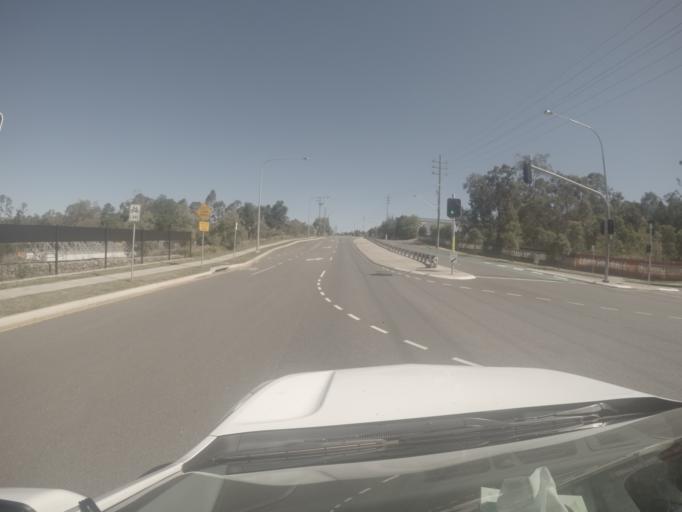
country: AU
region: Queensland
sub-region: Brisbane
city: Wacol
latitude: -27.5880
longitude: 152.9364
